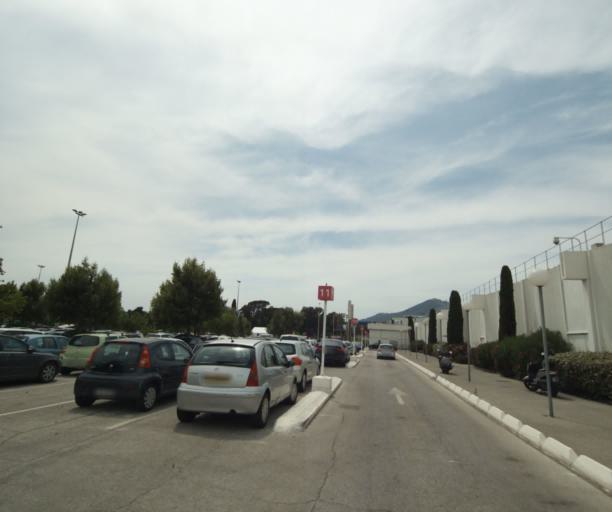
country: FR
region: Provence-Alpes-Cote d'Azur
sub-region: Departement du Var
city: La Garde
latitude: 43.1414
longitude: 6.0153
